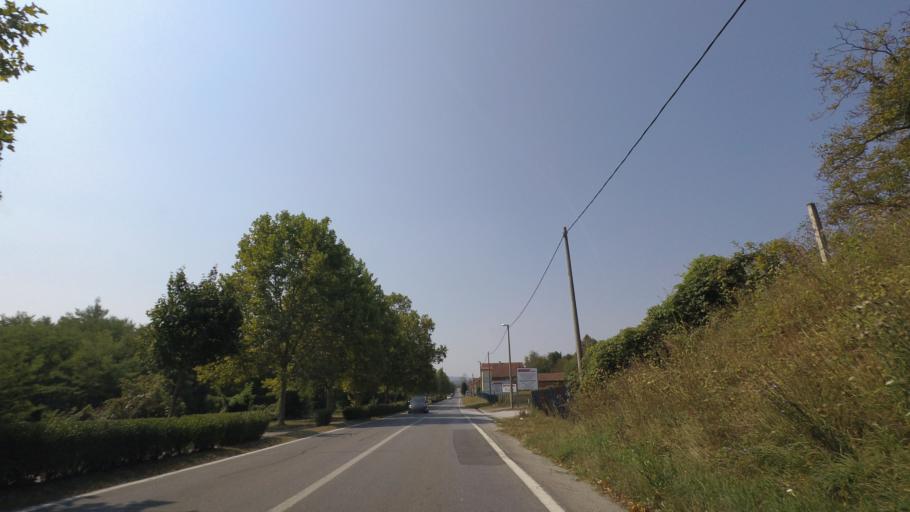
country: HR
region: Pozesko-Slavonska
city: Pakrac
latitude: 45.4250
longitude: 17.1813
